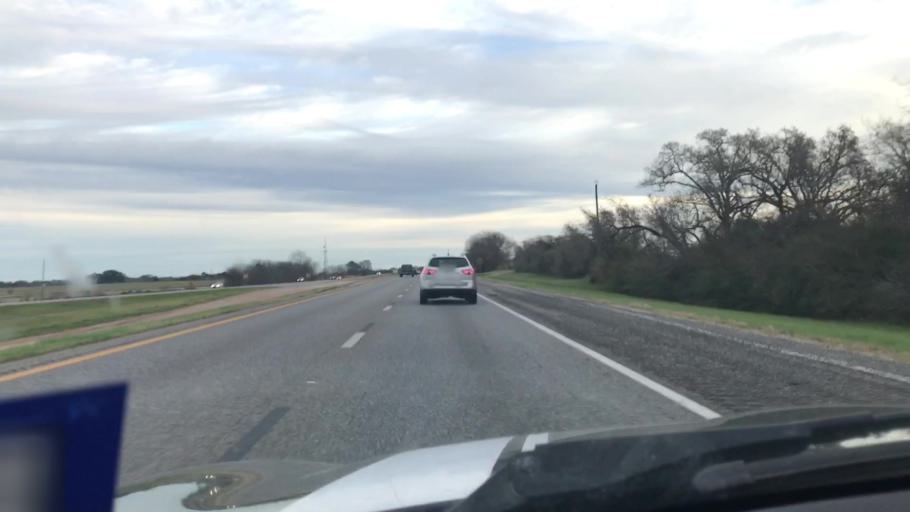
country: US
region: Texas
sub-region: Waller County
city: Hempstead
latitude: 30.1300
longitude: -96.1491
